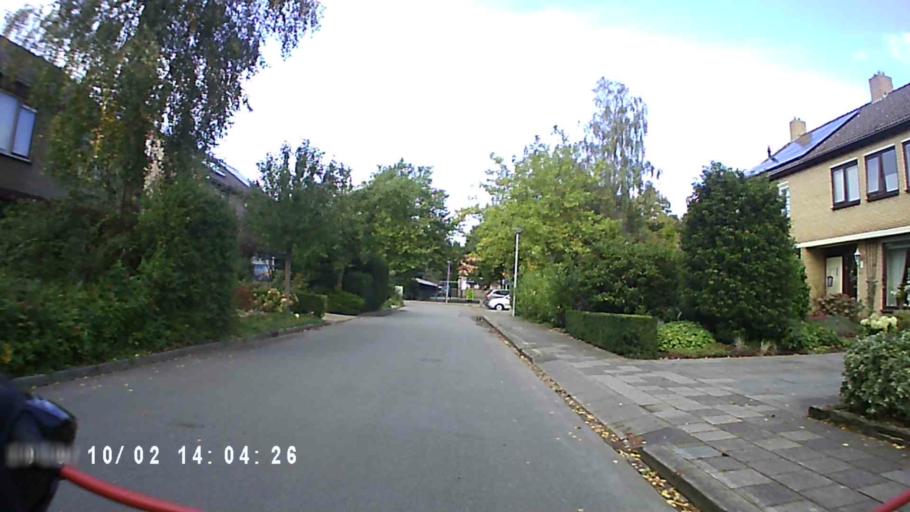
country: NL
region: Groningen
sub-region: Gemeente Zuidhorn
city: Zuidhorn
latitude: 53.2519
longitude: 6.3996
